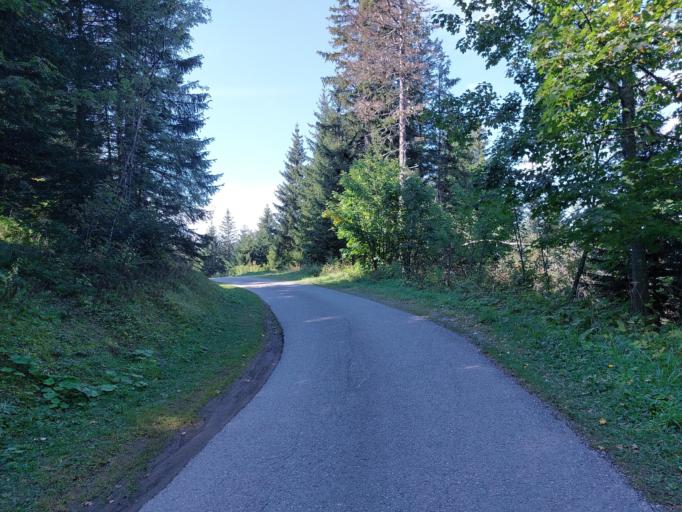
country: CH
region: Valais
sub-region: Monthey District
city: Troistorrents
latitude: 46.2182
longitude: 6.9494
